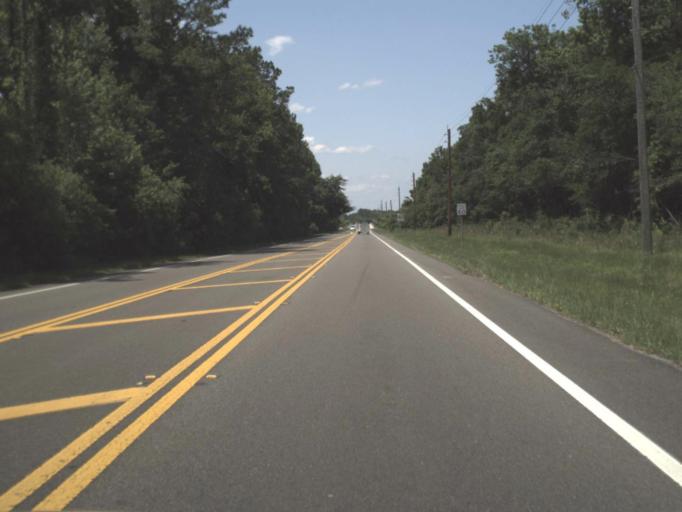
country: US
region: Florida
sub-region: Nassau County
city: Yulee
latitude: 30.5489
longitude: -81.6212
